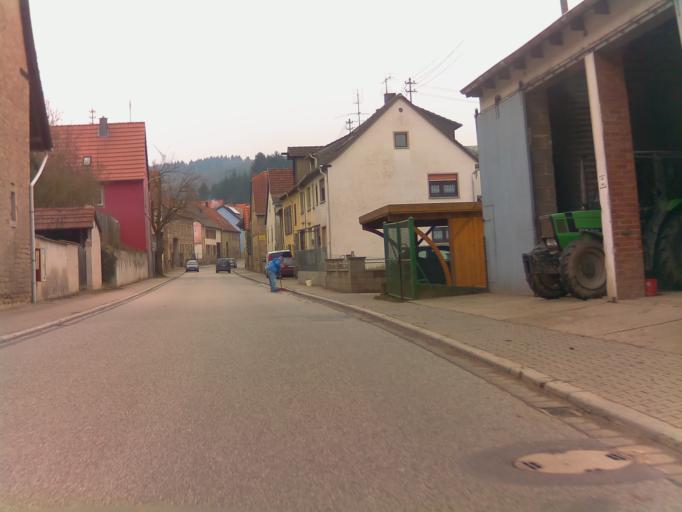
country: DE
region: Rheinland-Pfalz
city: Callbach
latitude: 49.7060
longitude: 7.6965
